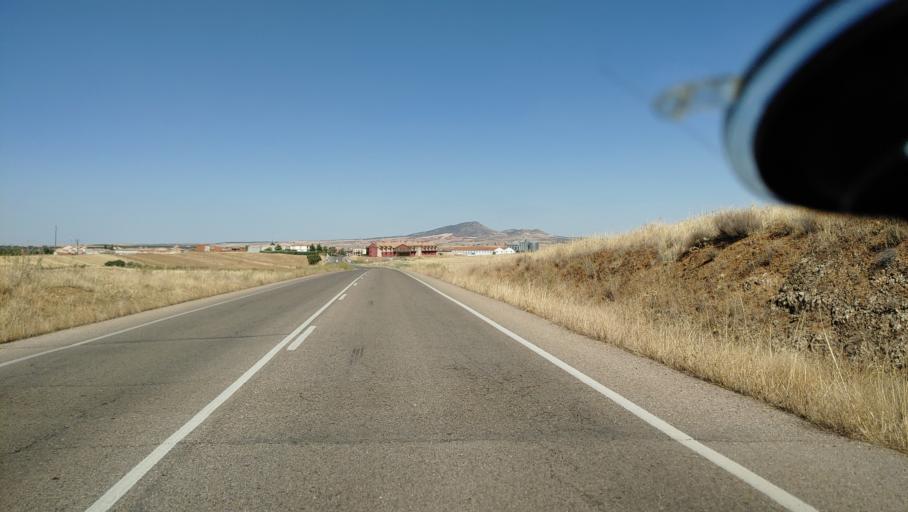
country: ES
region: Castille-La Mancha
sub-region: Province of Toledo
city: Pulgar
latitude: 39.6862
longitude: -4.1645
